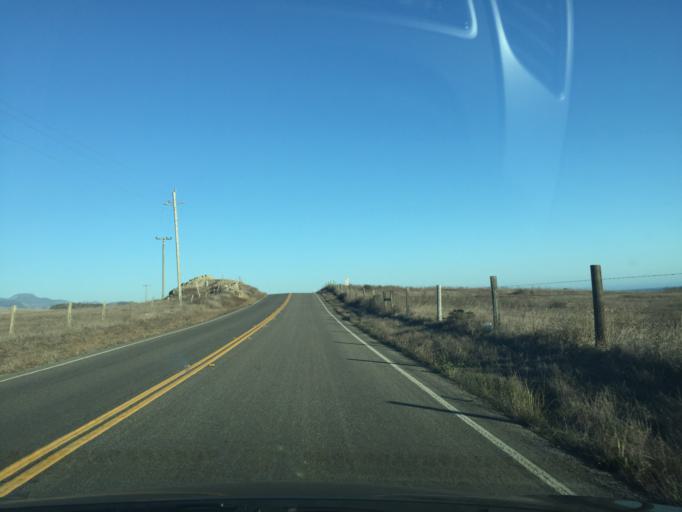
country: US
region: California
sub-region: San Luis Obispo County
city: Cambria
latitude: 35.6693
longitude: -121.2762
